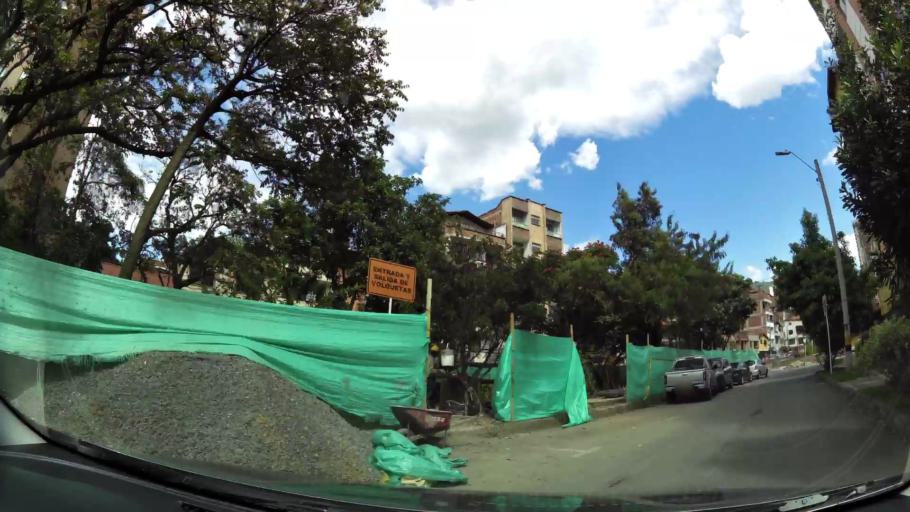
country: CO
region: Antioquia
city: Sabaneta
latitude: 6.1525
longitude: -75.6201
